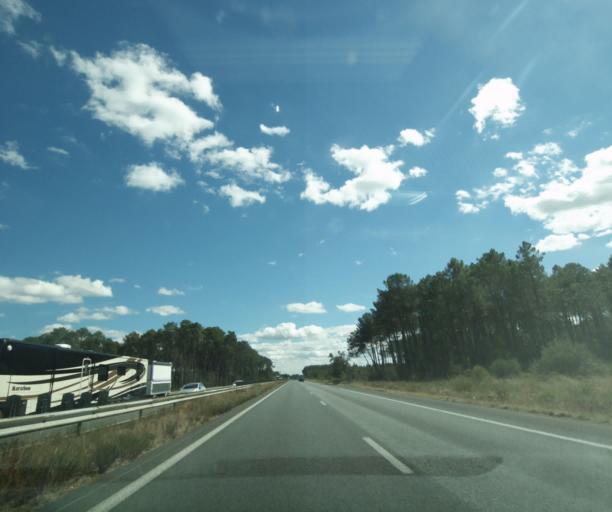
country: FR
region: Aquitaine
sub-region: Departement de la Gironde
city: Illats
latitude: 44.6318
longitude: -0.4126
